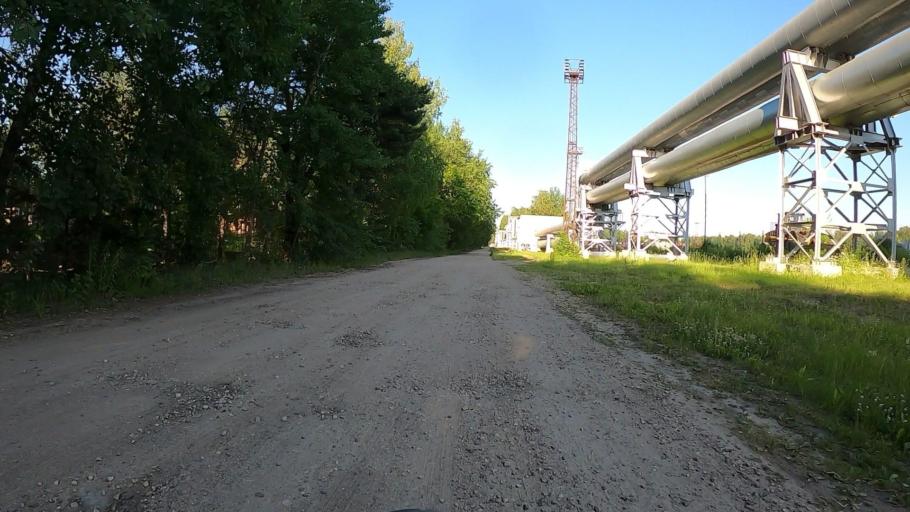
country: LV
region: Stopini
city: Ulbroka
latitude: 56.9226
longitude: 24.2282
